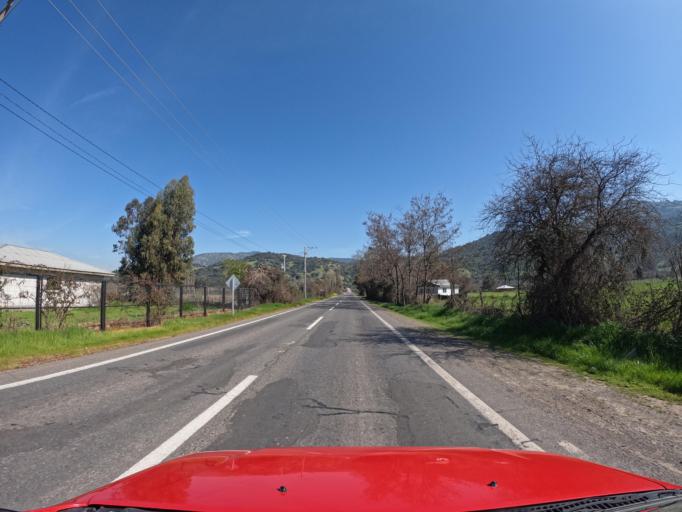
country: CL
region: Maule
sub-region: Provincia de Curico
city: Rauco
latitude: -34.9815
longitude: -71.4154
